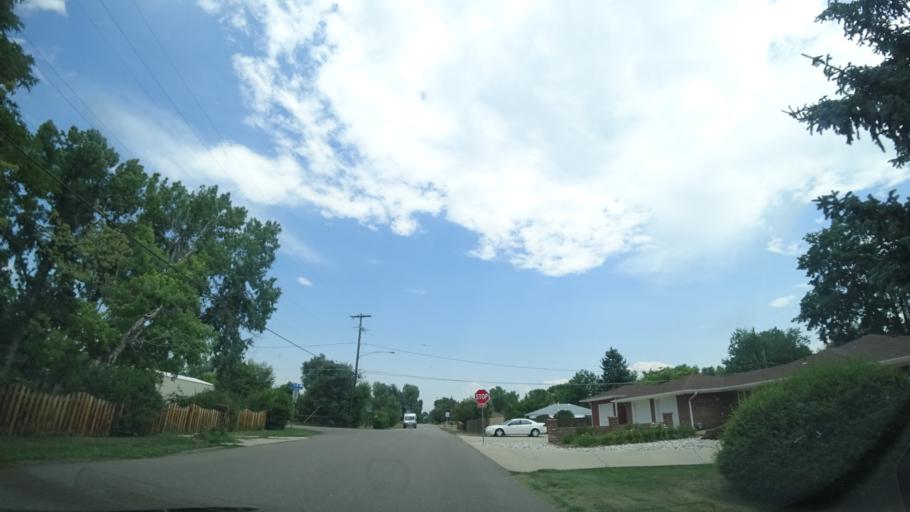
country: US
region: Colorado
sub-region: Jefferson County
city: Lakewood
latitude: 39.7221
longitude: -105.0870
